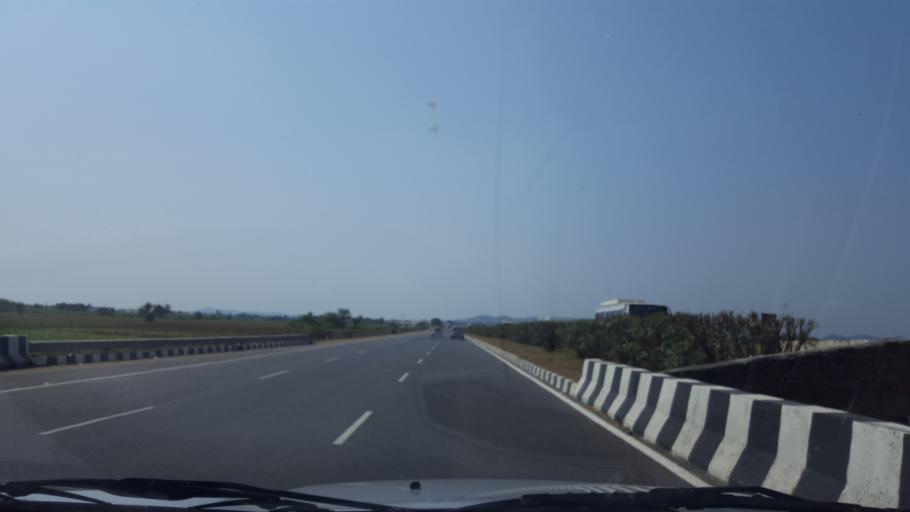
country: IN
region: Andhra Pradesh
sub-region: Guntur
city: Chilakalurupet
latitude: 16.0191
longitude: 80.1222
